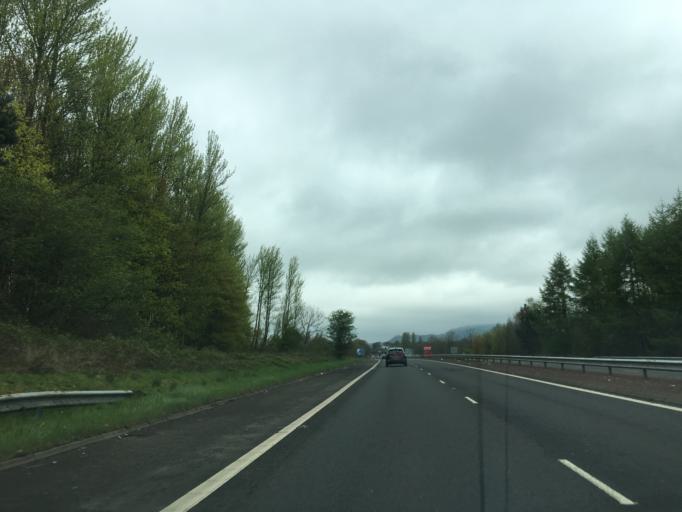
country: GB
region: Scotland
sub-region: Renfrewshire
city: Bishopton
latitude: 55.9005
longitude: -4.4848
